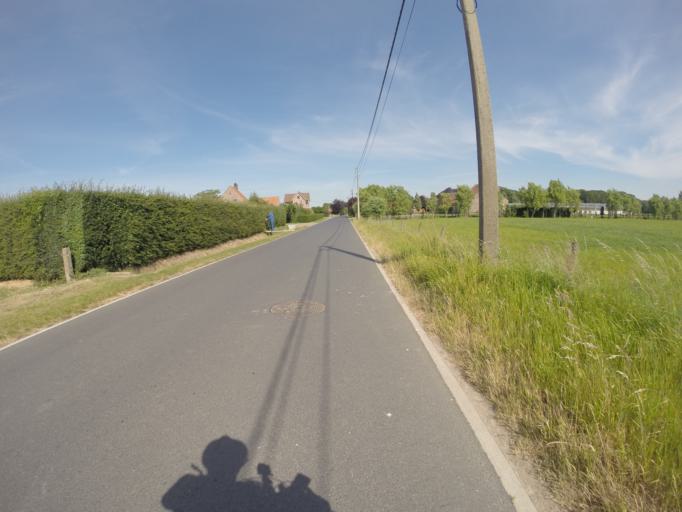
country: BE
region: Flanders
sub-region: Provincie Oost-Vlaanderen
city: Knesselare
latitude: 51.1714
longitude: 3.3834
